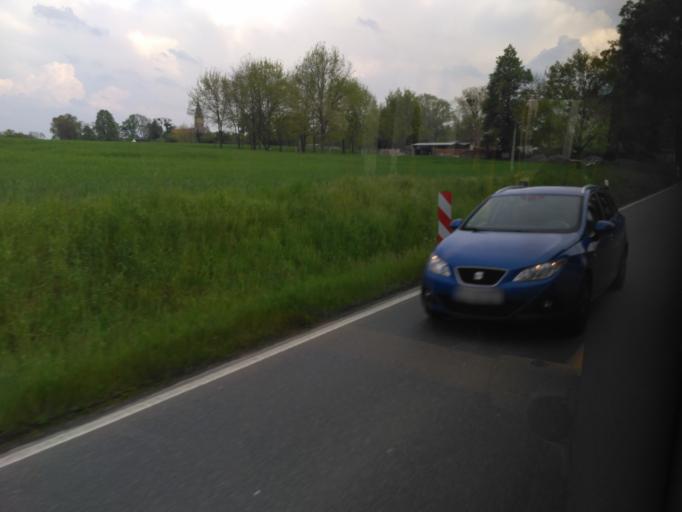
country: DE
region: Saxony
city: Konigsbruck
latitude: 51.3000
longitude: 13.9148
